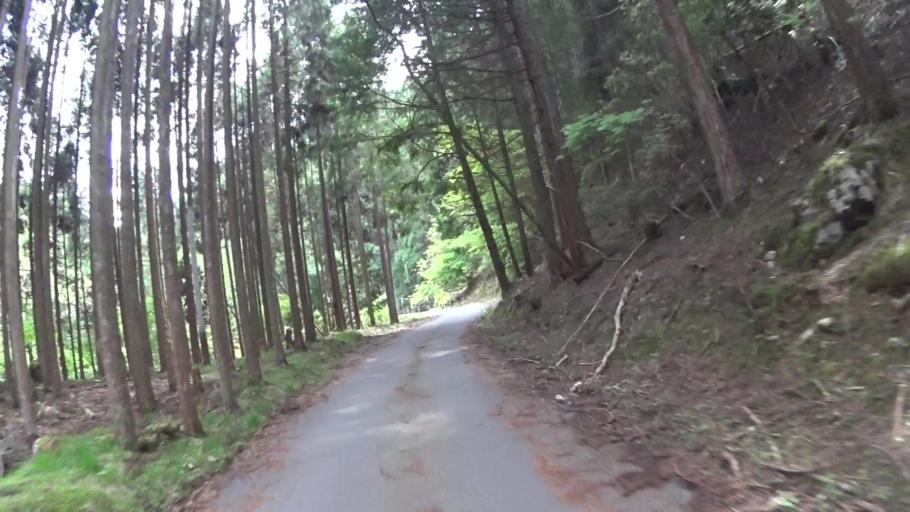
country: JP
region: Kyoto
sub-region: Kyoto-shi
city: Kamigyo-ku
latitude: 35.1898
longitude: 135.7031
